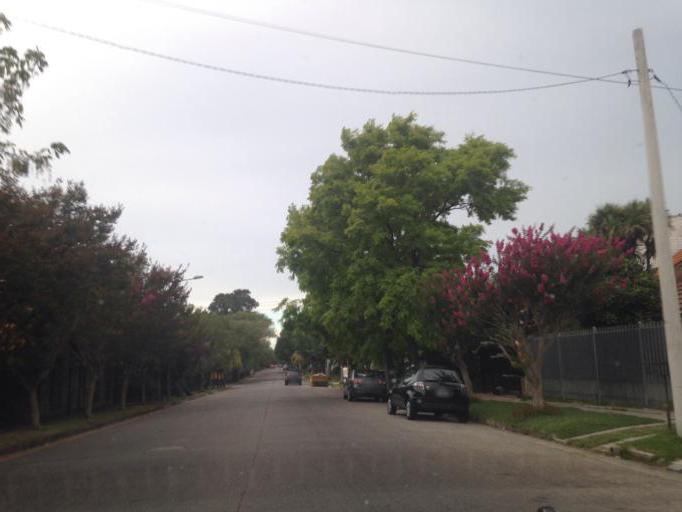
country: AR
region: Buenos Aires
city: Mar del Plata
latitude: -38.0254
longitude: -57.5467
